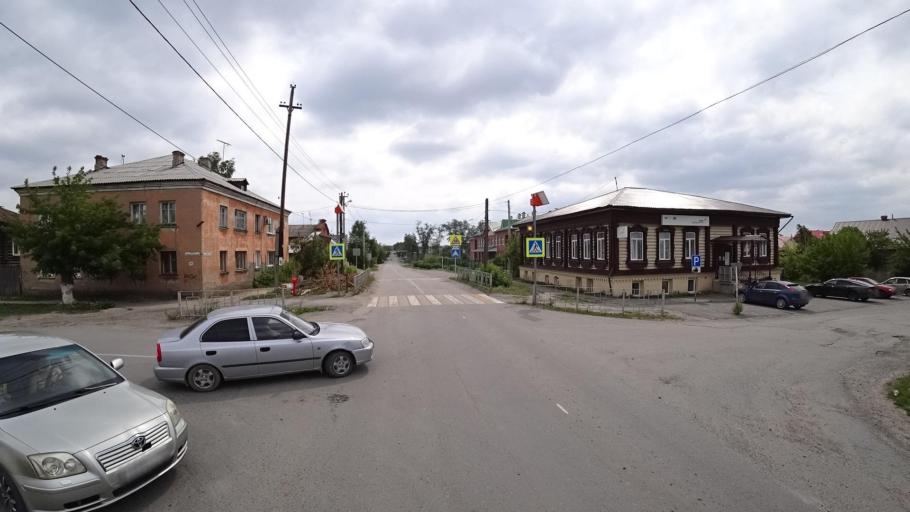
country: RU
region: Sverdlovsk
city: Kamyshlov
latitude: 56.8390
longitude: 62.7106
